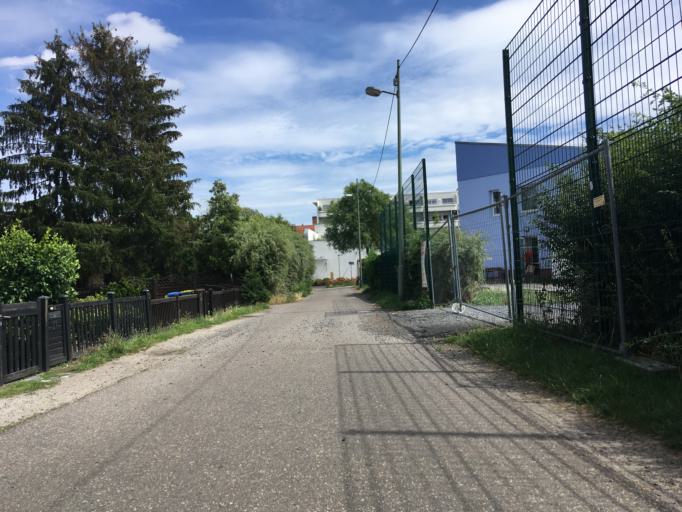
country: DE
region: Berlin
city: Altglienicke
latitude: 52.4195
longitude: 13.5361
